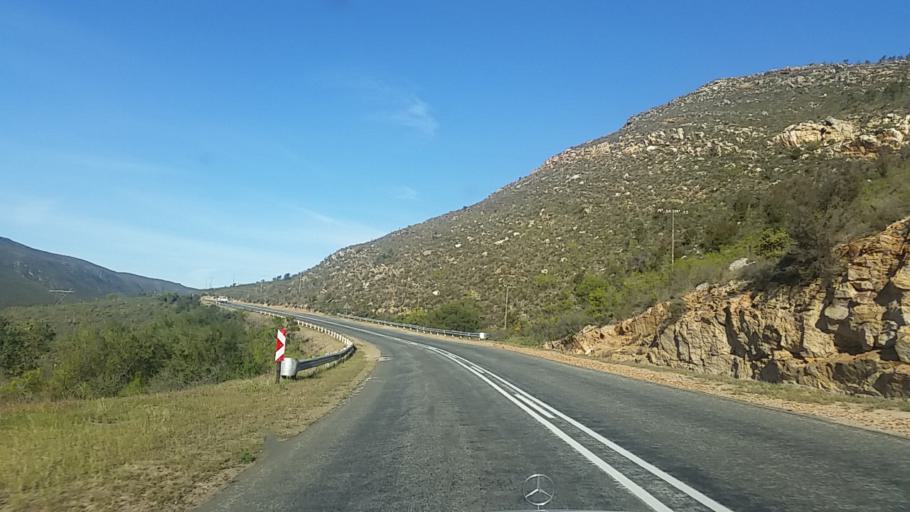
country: ZA
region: Western Cape
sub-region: Eden District Municipality
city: Knysna
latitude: -33.7482
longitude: 22.9782
